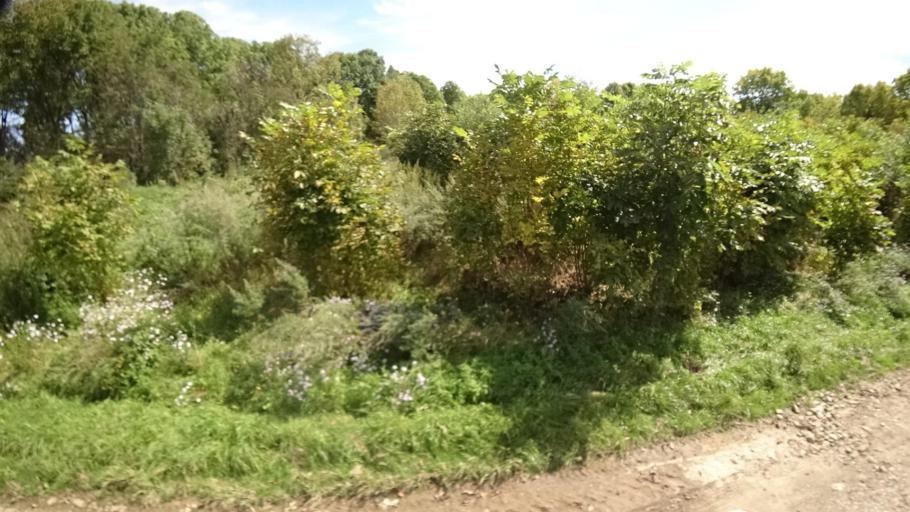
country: RU
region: Primorskiy
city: Kirovskiy
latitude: 44.7564
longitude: 133.6114
